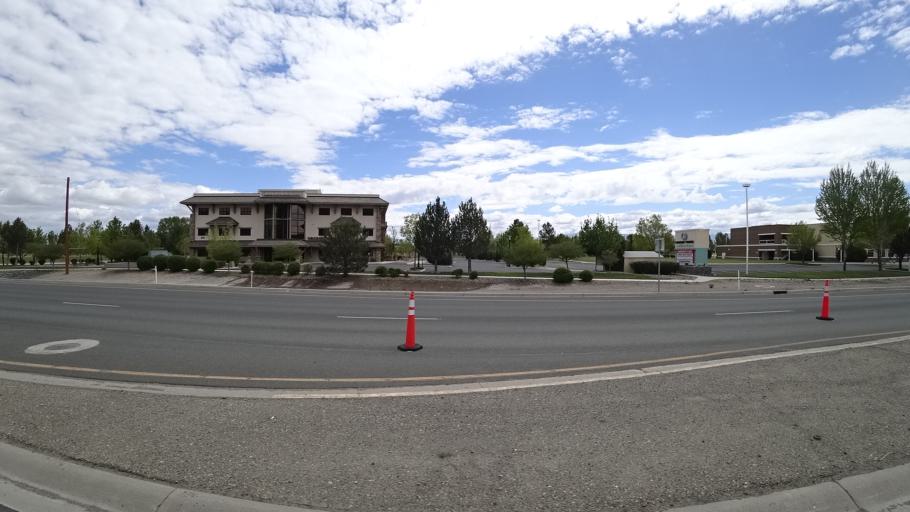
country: US
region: Nevada
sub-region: Douglas County
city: Minden
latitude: 38.9637
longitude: -119.7792
